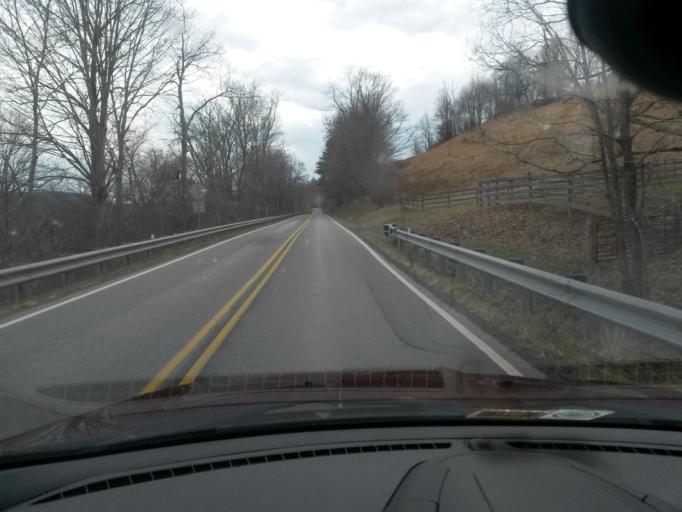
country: US
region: Virginia
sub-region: Highland County
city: Monterey
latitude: 38.3679
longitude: -79.6263
